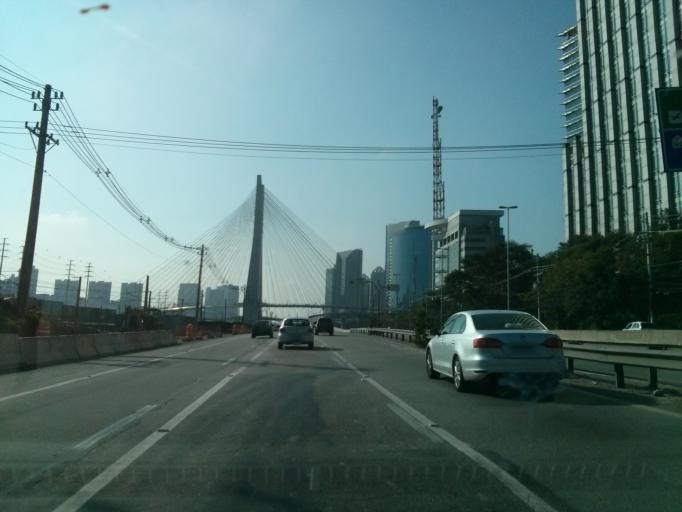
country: BR
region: Sao Paulo
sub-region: Taboao Da Serra
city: Taboao da Serra
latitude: -23.6176
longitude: -46.6997
